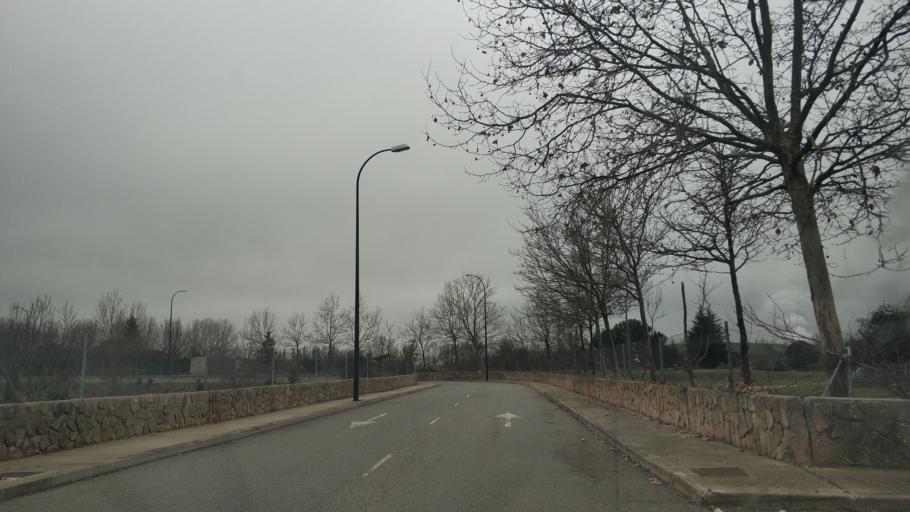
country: ES
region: Castille and Leon
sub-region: Provincia de Salamanca
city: Villamayor
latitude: 40.9961
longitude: -5.7276
